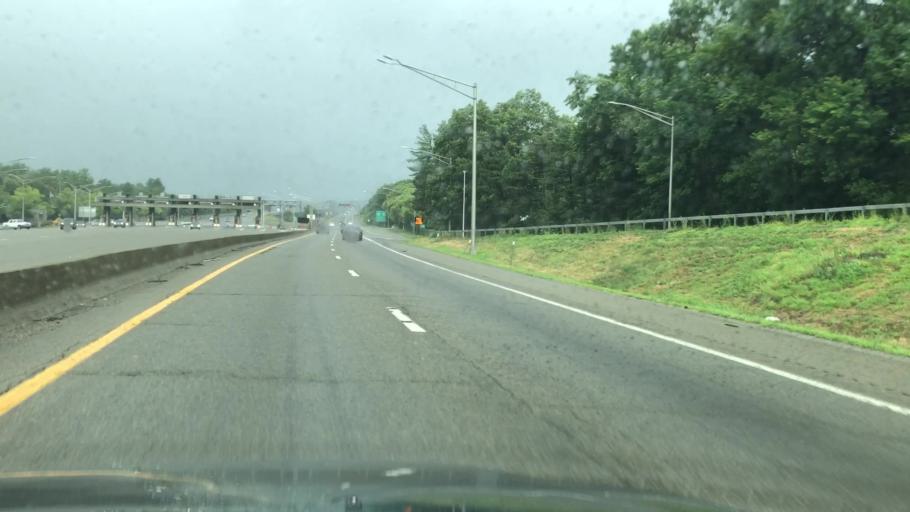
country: US
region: New York
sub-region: Dutchess County
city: Beacon
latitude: 41.5179
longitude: -73.9757
